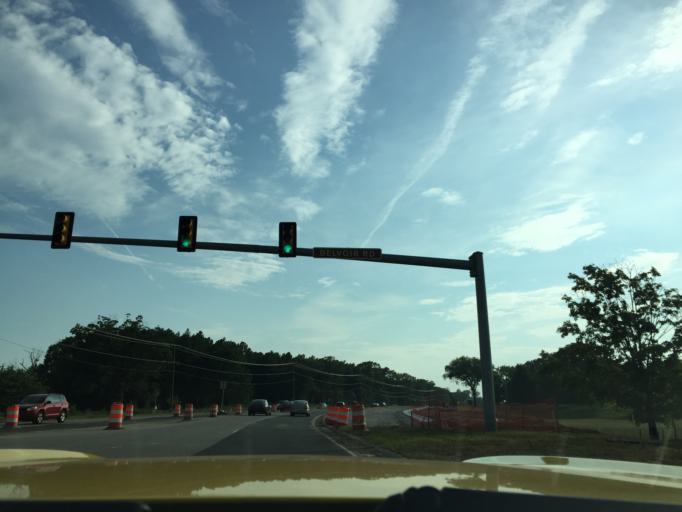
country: US
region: Virginia
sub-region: Fairfax County
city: Fort Belvoir
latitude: 38.7119
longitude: -77.1437
